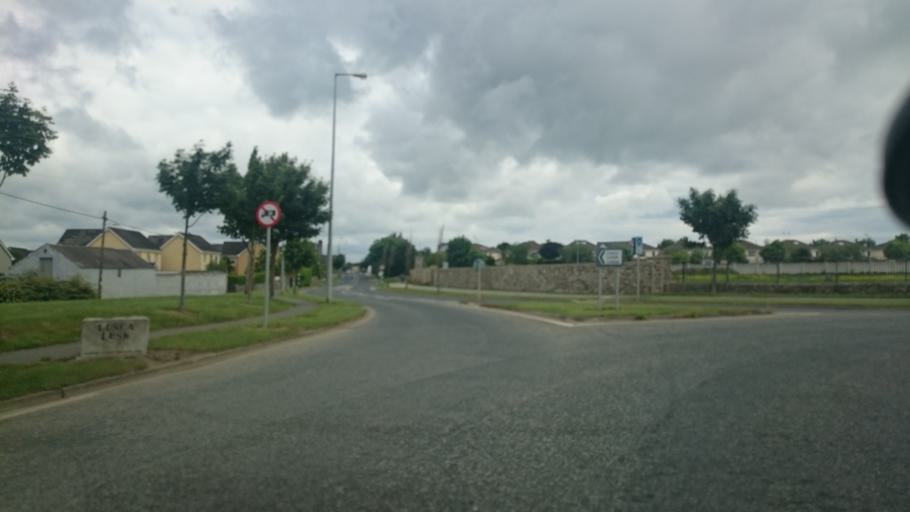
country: IE
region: Leinster
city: Lusk
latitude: 53.5206
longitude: -6.1686
